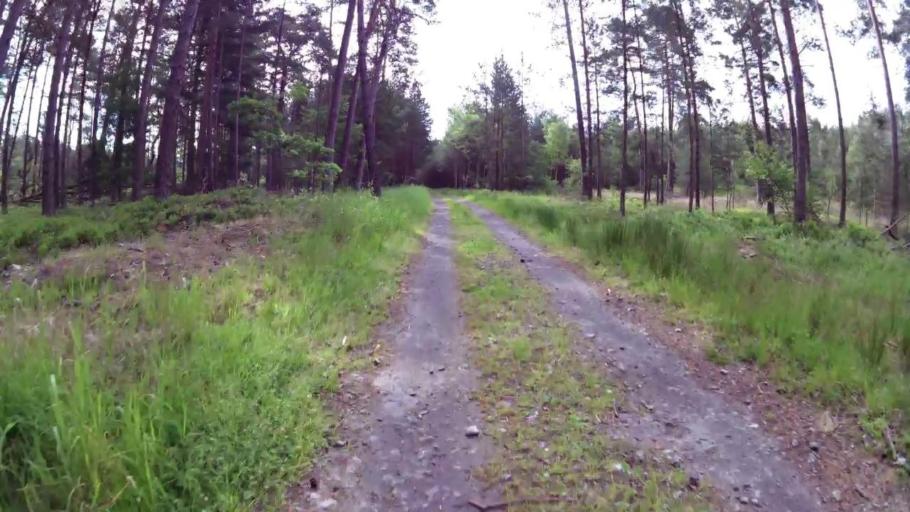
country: PL
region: West Pomeranian Voivodeship
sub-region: Swinoujscie
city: Swinoujscie
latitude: 53.9082
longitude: 14.3179
